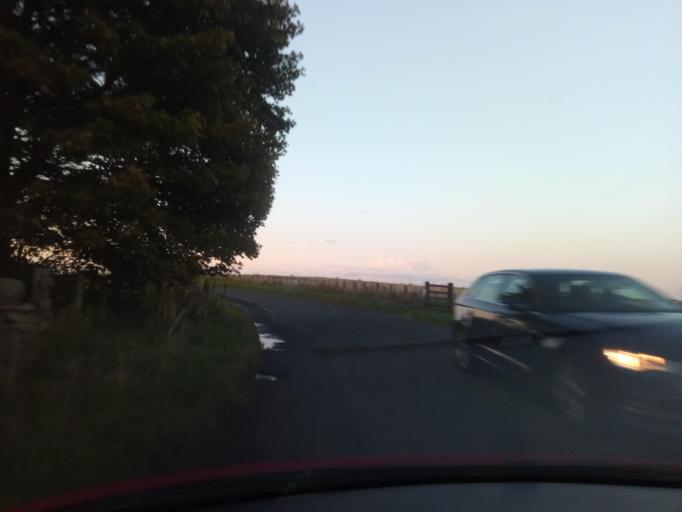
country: GB
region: Scotland
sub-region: East Lothian
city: Pencaitland
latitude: 55.8146
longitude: -2.8749
